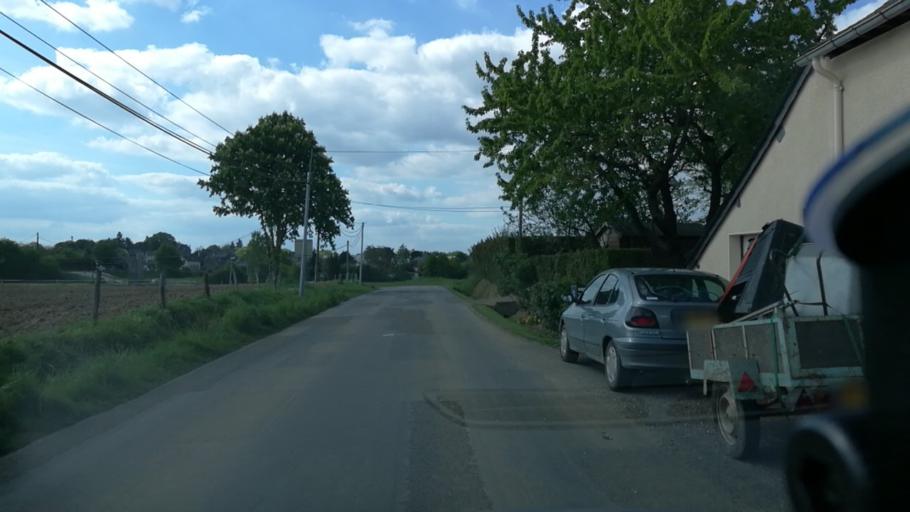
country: FR
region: Brittany
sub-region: Departement d'Ille-et-Vilaine
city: Retiers
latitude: 47.9047
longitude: -1.3714
